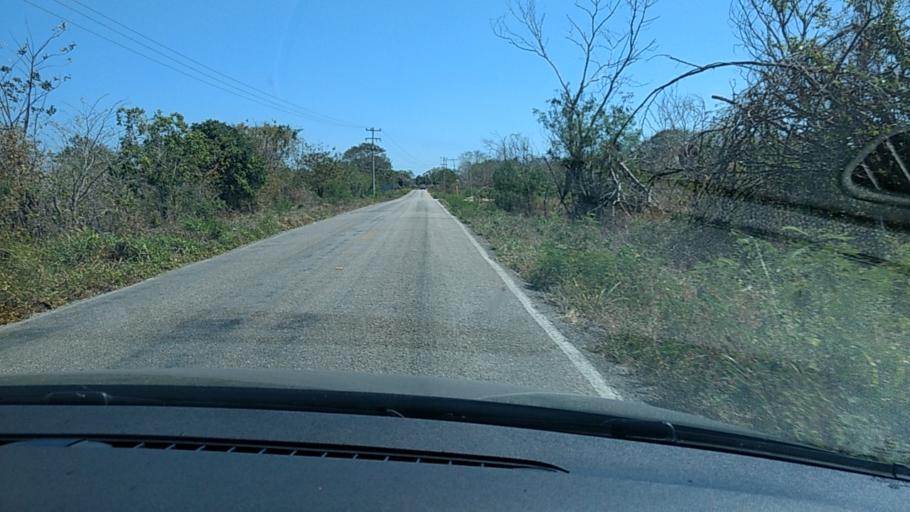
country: MX
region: Yucatan
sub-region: Tizimin
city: Tizimin
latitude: 21.1945
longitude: -88.1714
